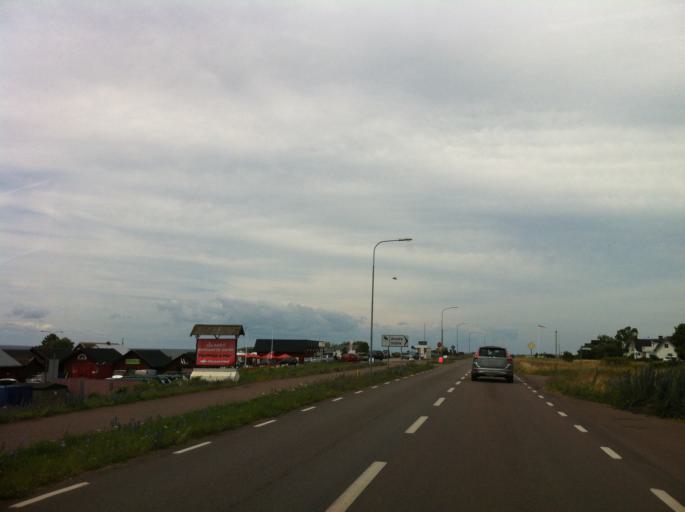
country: SE
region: Kalmar
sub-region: Oskarshamns Kommun
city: Oskarshamn
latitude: 57.3278
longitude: 17.0085
